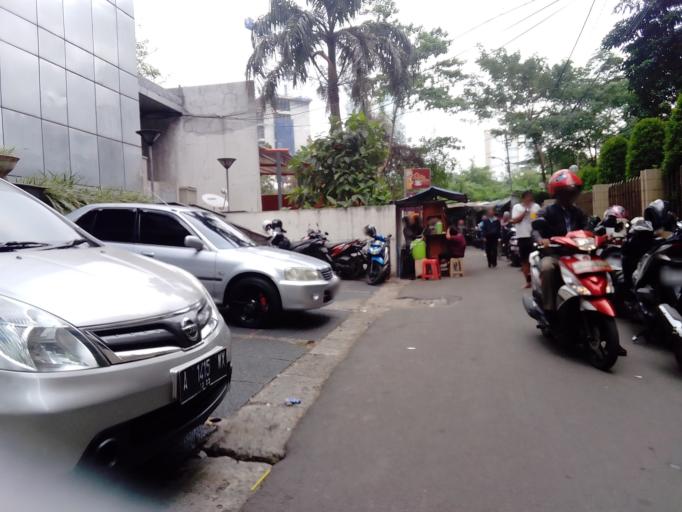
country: ID
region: Jakarta Raya
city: Jakarta
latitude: -6.1962
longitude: 106.8212
